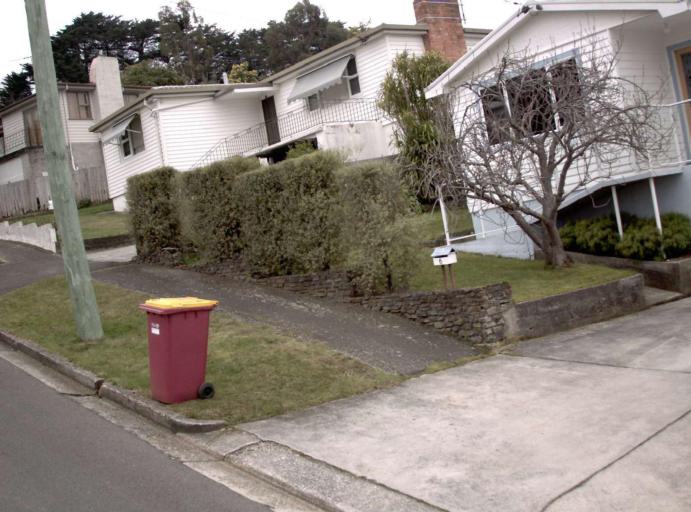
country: AU
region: Tasmania
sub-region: Launceston
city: East Launceston
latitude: -41.4579
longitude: 147.1590
